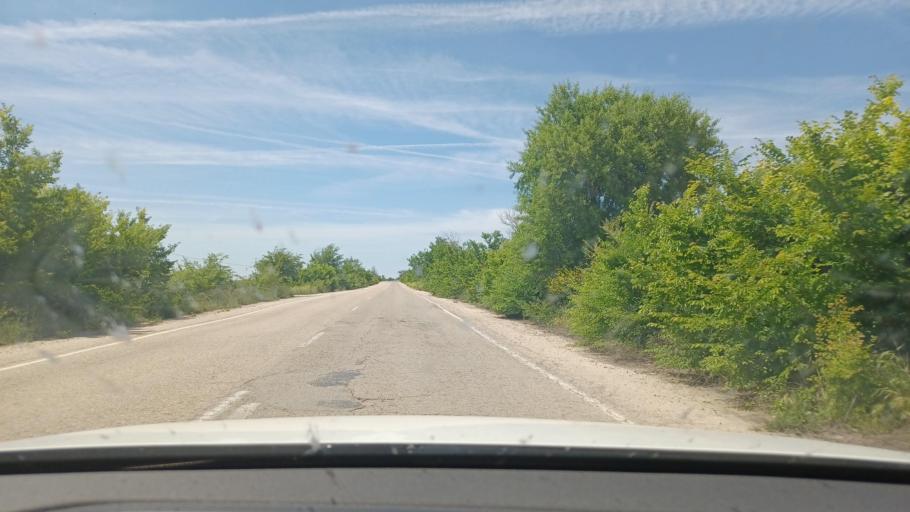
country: ES
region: Castille-La Mancha
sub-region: Provincia de Cuenca
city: Montalbo
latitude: 39.8819
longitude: -2.6754
